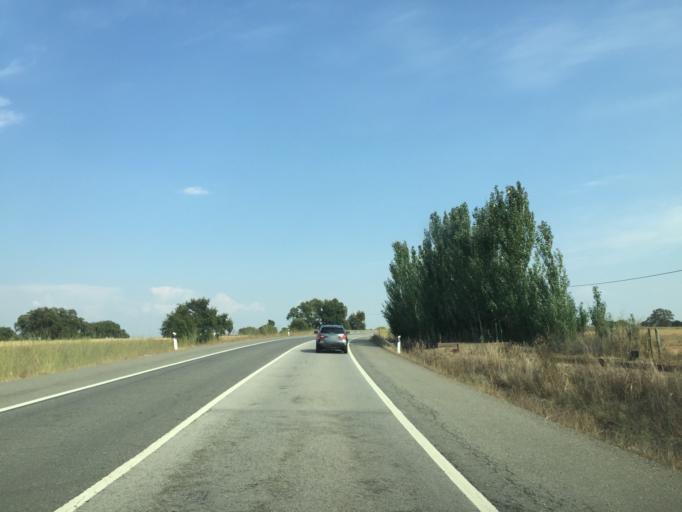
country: PT
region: Beja
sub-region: Aljustrel
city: Aljustrel
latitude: 37.9373
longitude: -8.3634
